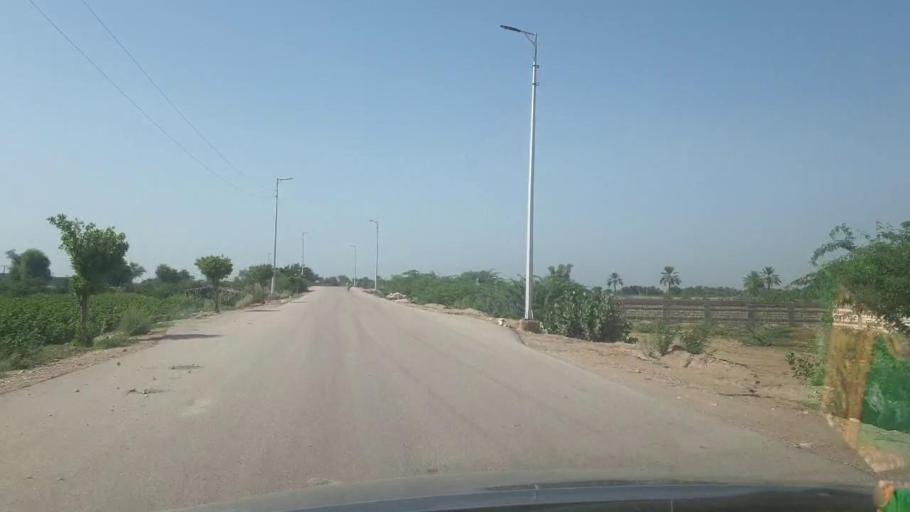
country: PK
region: Sindh
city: Rohri
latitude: 27.5135
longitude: 69.0356
